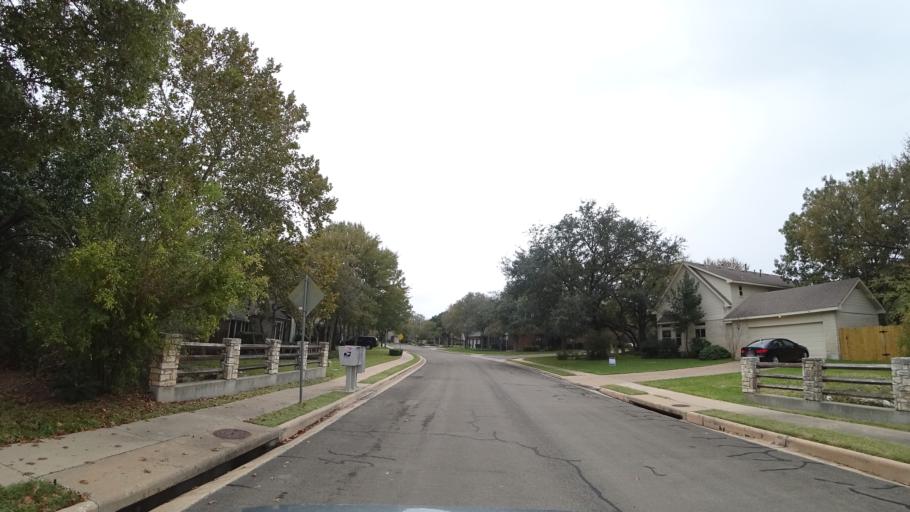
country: US
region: Texas
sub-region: Williamson County
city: Round Rock
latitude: 30.5165
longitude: -97.7040
